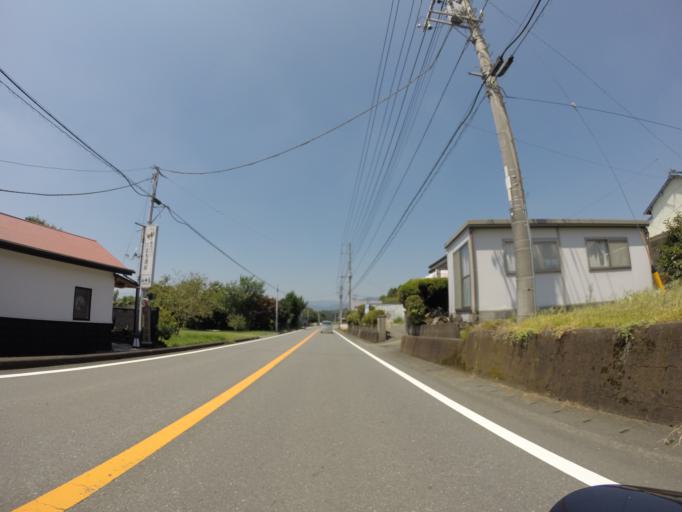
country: JP
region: Shizuoka
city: Fujinomiya
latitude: 35.2702
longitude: 138.6212
